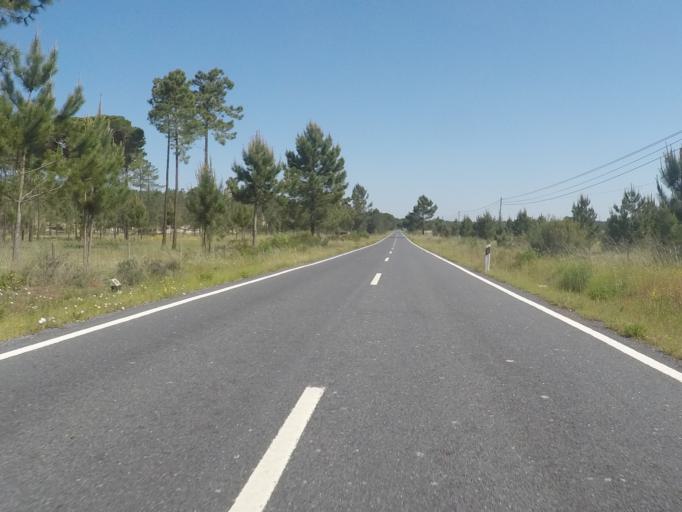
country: PT
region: Setubal
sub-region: Grandola
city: Grandola
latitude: 38.2880
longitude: -8.7264
